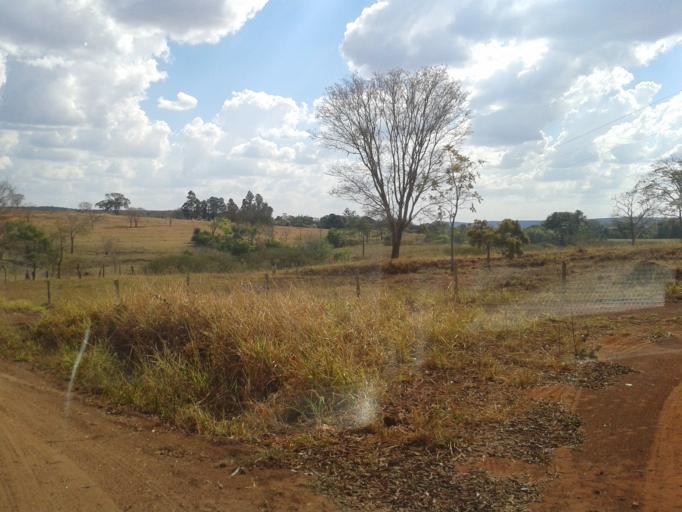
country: BR
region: Minas Gerais
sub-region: Santa Vitoria
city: Santa Vitoria
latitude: -19.2020
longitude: -49.8937
